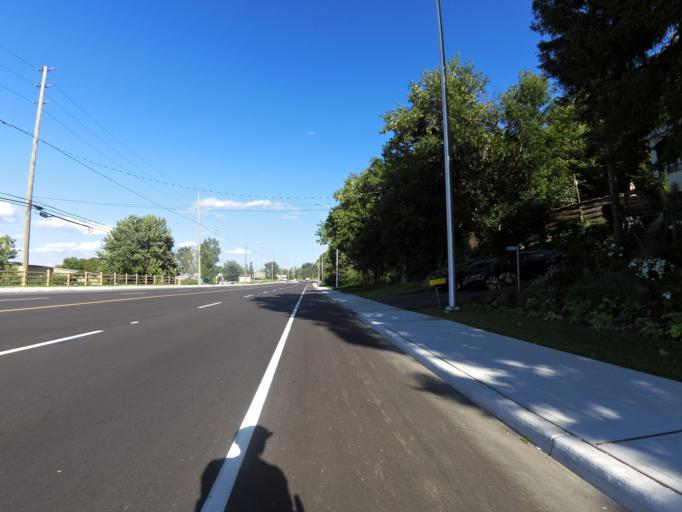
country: CA
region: Ontario
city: Clarence-Rockland
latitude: 45.4882
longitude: -75.4842
